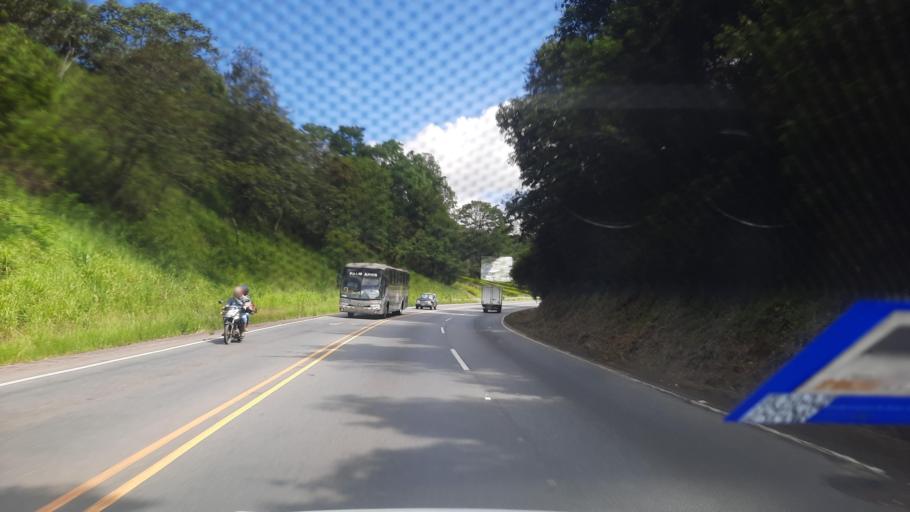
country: CR
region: Alajuela
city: Naranjo
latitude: 10.0698
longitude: -84.3700
